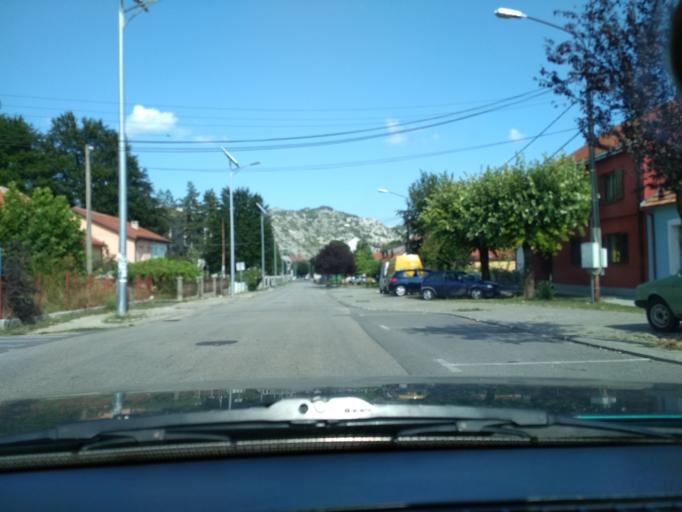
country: ME
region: Cetinje
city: Cetinje
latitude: 42.3935
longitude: 18.9131
